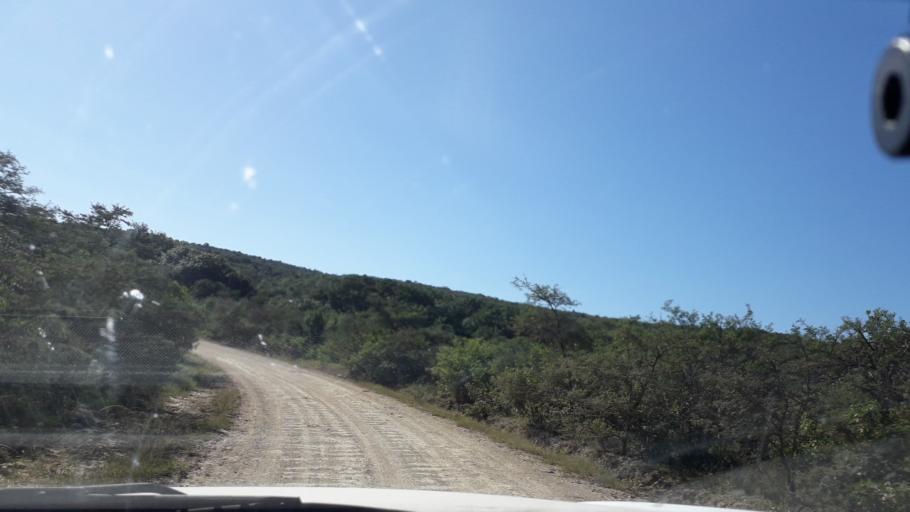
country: ZA
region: Eastern Cape
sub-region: Amathole District Municipality
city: Komga
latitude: -32.7685
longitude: 27.9625
